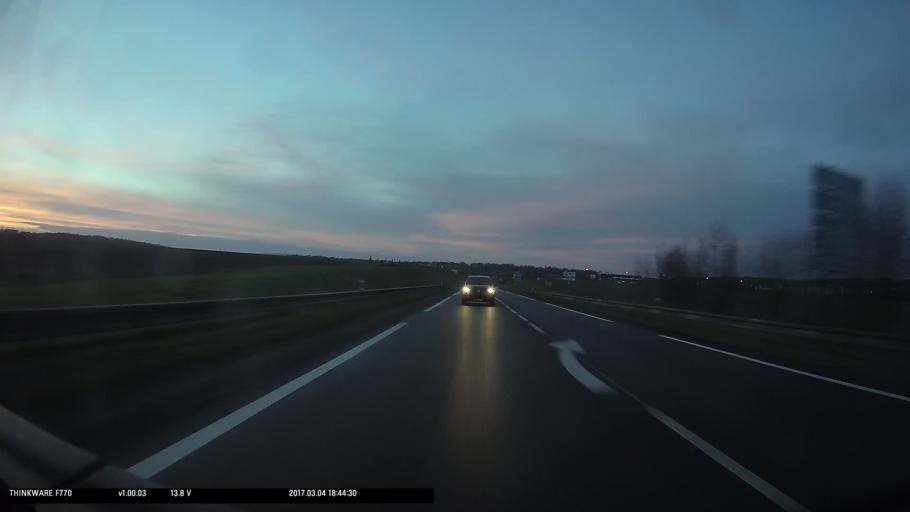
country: FR
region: Ile-de-France
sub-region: Departement du Val-d'Oise
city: Marines
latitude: 49.1382
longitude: 1.9697
